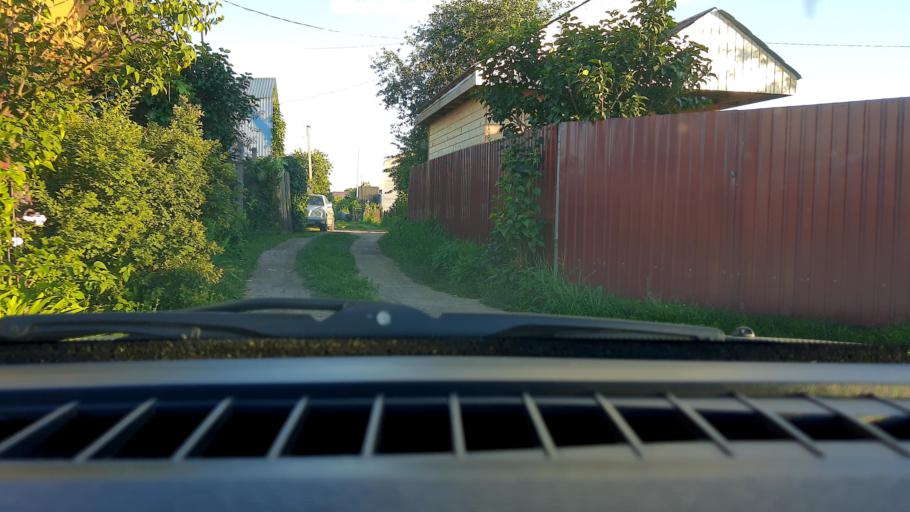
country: RU
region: Nizjnij Novgorod
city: Afonino
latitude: 56.2210
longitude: 44.1008
